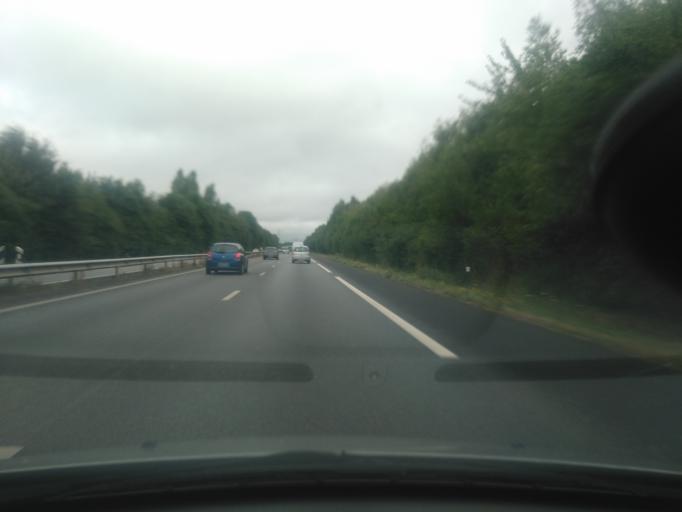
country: FR
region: Brittany
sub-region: Departement d'Ille-et-Vilaine
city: Montgermont
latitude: 48.1667
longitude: -1.7109
